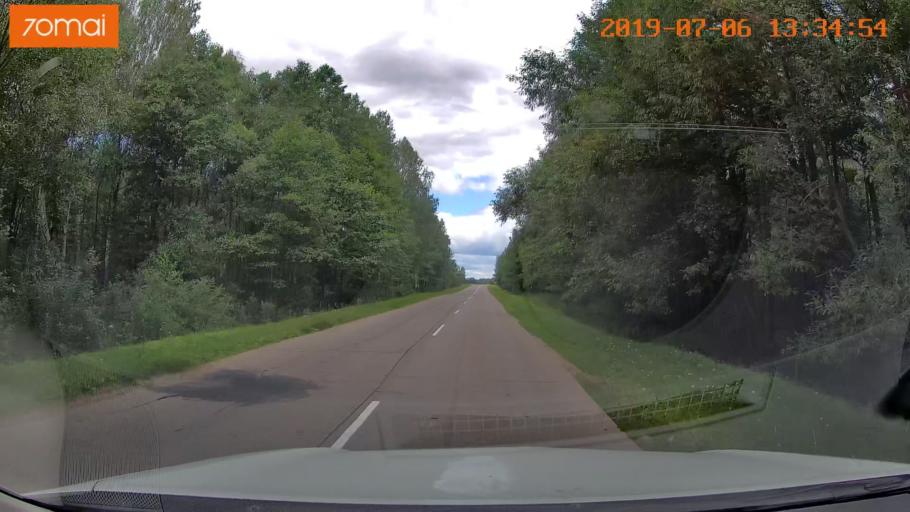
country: BY
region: Minsk
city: Enyerhyetykaw
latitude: 53.6780
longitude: 26.8903
